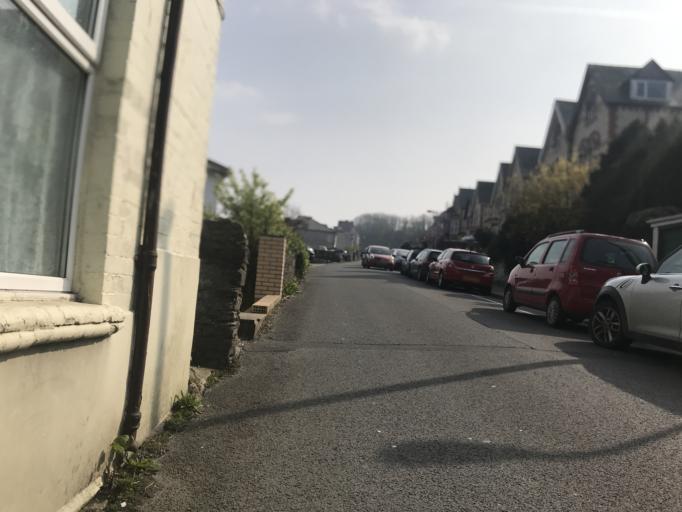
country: GB
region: England
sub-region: Devon
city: Ilfracombe
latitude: 51.2041
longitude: -4.1271
